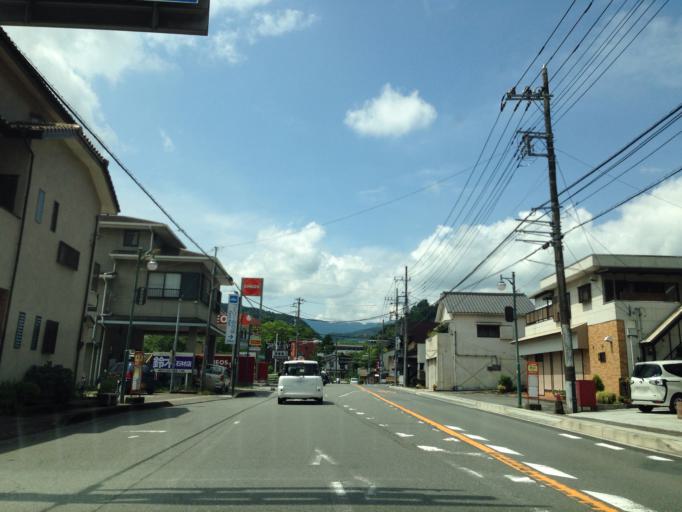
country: JP
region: Shizuoka
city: Heda
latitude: 34.9294
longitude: 138.9331
